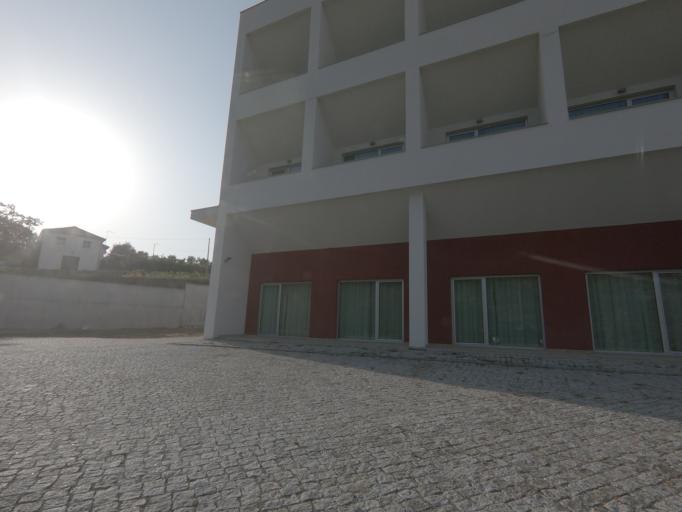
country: PT
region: Viseu
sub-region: Tabuaco
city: Tabuaco
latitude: 41.1193
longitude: -7.5835
